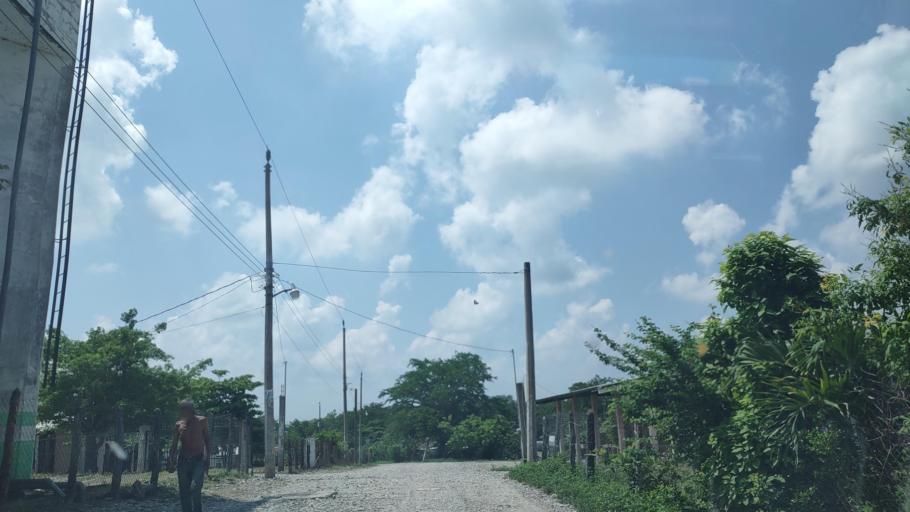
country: MX
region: Veracruz
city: Tempoal de Sanchez
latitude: 21.5483
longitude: -98.2750
